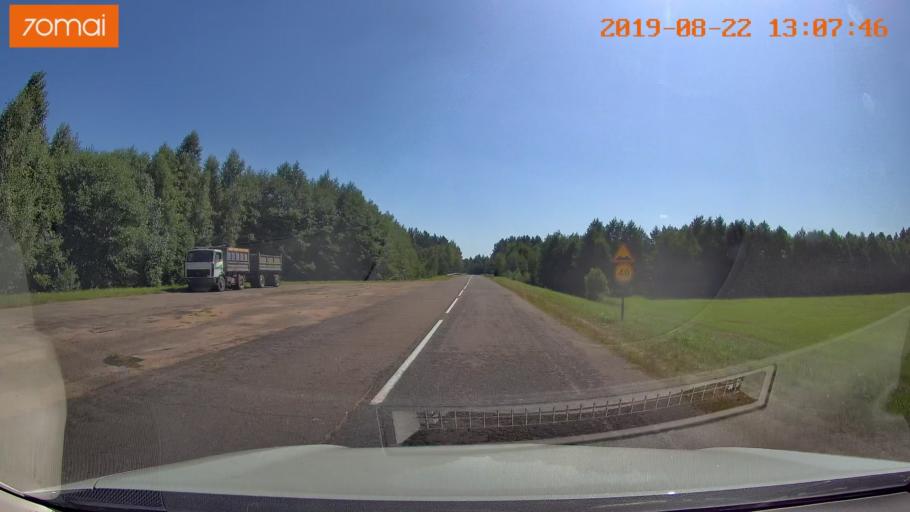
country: BY
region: Minsk
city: Prawdzinski
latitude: 53.3324
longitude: 27.8386
